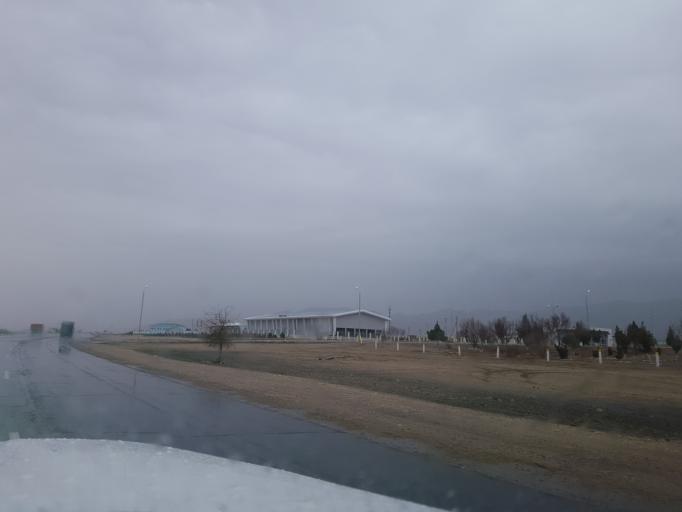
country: TM
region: Balkan
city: Balkanabat
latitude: 39.5424
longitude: 54.2979
